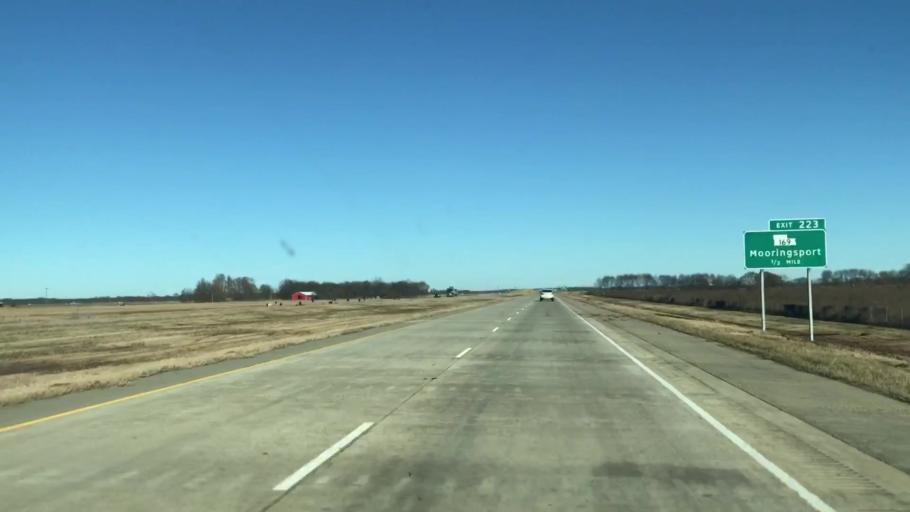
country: US
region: Louisiana
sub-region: Bossier Parish
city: Benton
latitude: 32.6900
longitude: -93.8562
